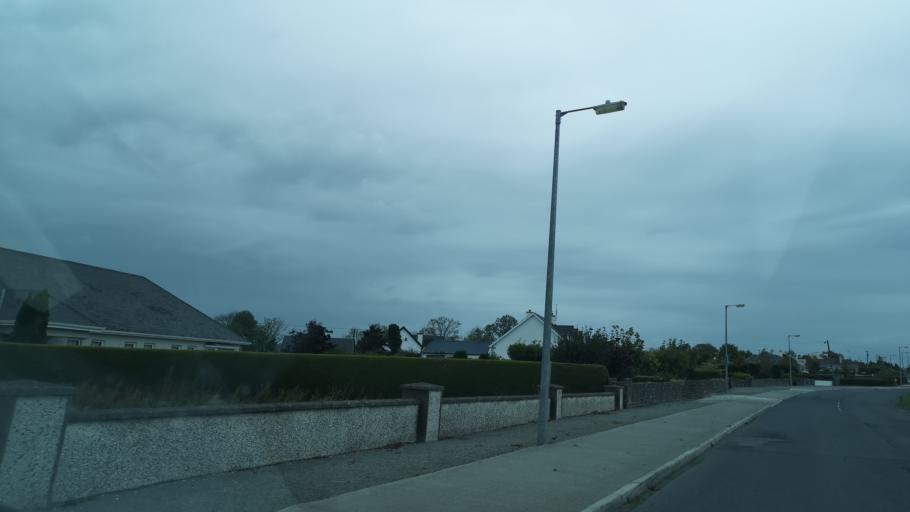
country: IE
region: Leinster
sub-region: Uibh Fhaili
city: Banagher
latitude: 53.1959
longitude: -7.9746
